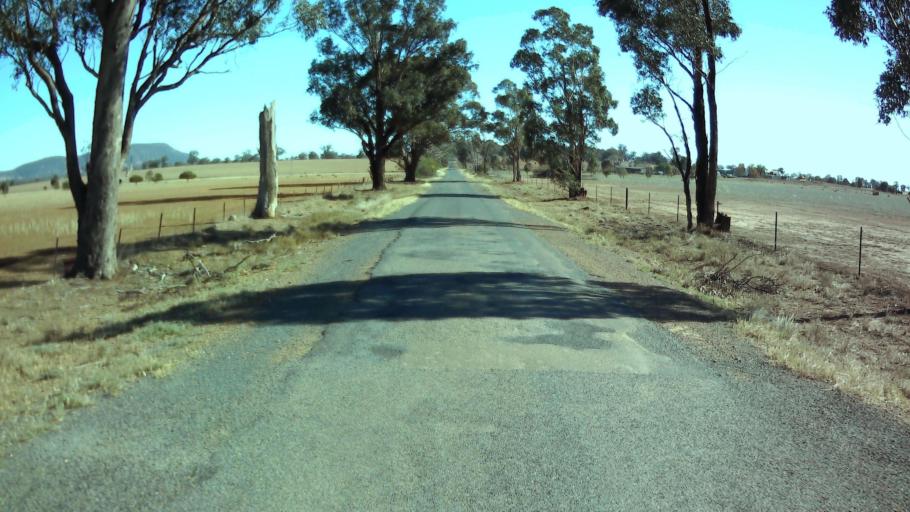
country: AU
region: New South Wales
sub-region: Weddin
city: Grenfell
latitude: -33.7958
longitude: 147.9566
